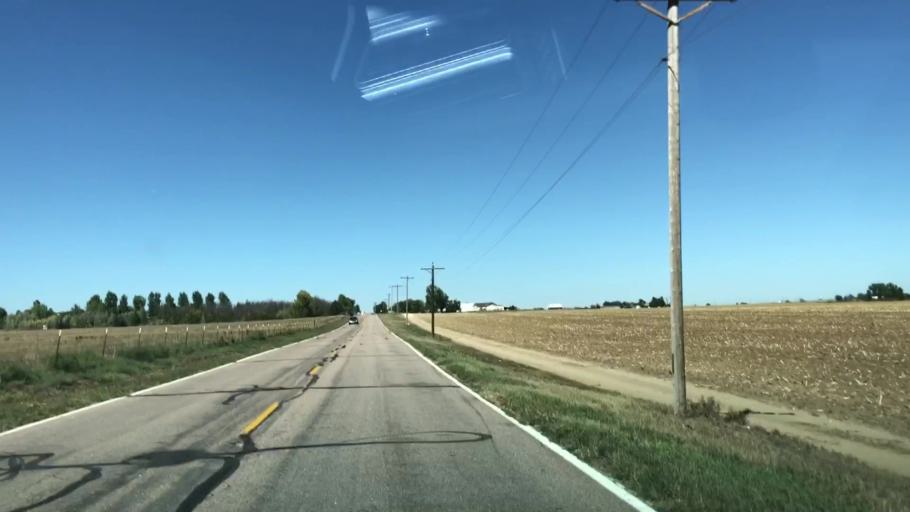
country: US
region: Colorado
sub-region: Weld County
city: Windsor
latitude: 40.5263
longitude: -104.9270
